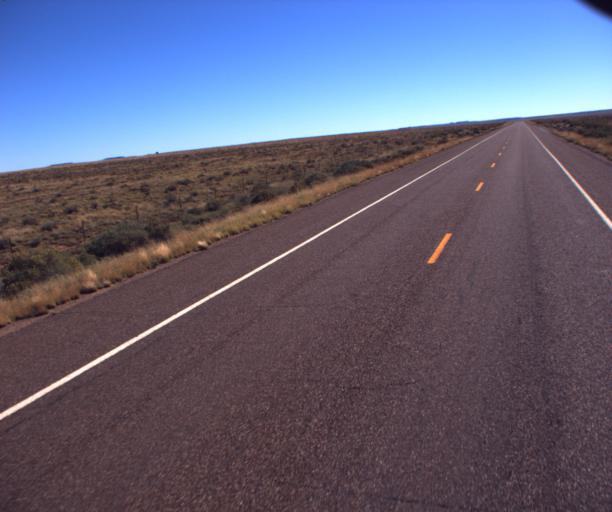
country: US
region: Arizona
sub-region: Navajo County
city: Holbrook
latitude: 34.8588
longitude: -110.0009
